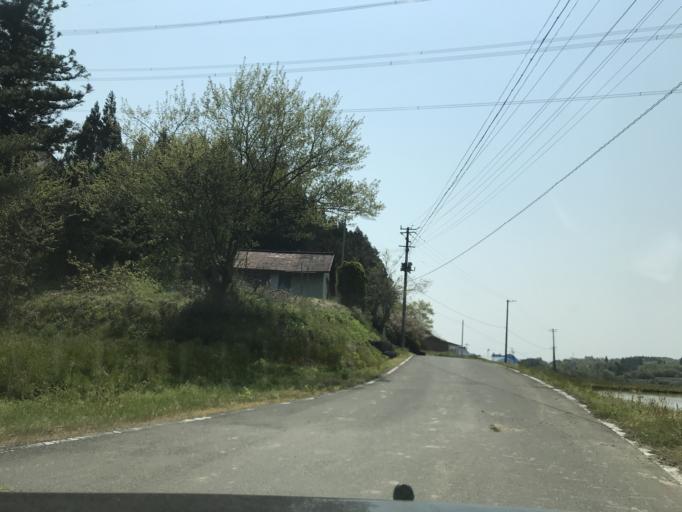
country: JP
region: Iwate
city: Ichinoseki
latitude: 38.8558
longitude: 141.0860
